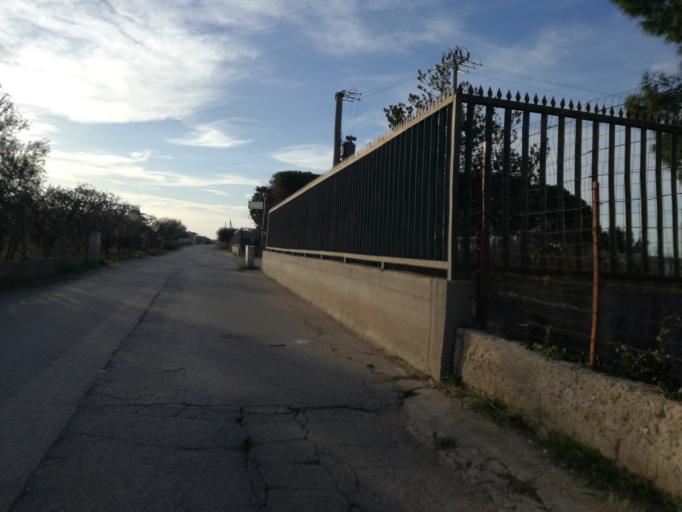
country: IT
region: Apulia
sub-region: Provincia di Bari
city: Capurso
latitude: 41.0497
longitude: 16.9075
